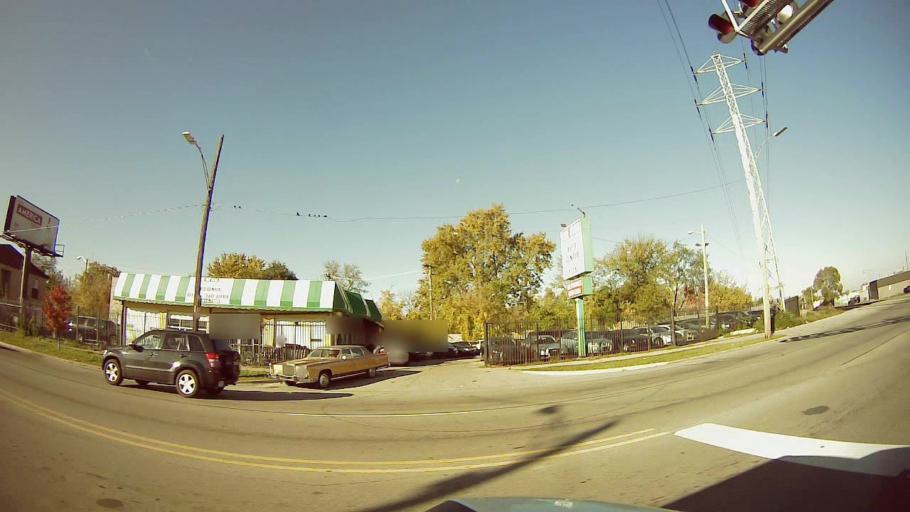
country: US
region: Michigan
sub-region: Wayne County
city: Dearborn
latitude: 42.3493
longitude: -83.1965
